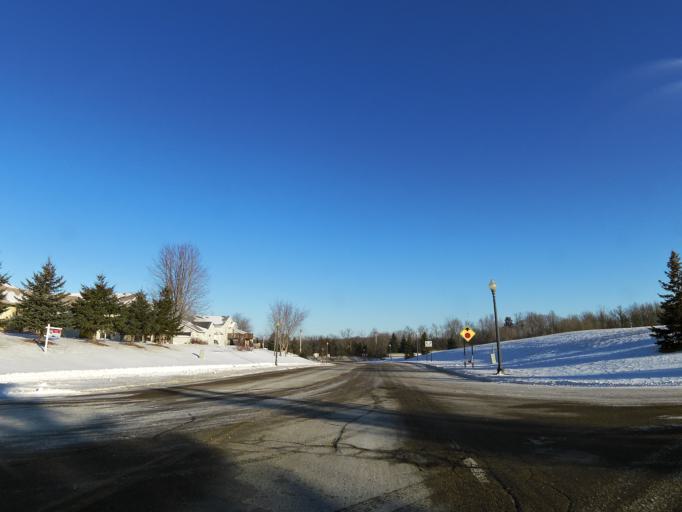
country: US
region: Minnesota
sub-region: Scott County
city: Jordan
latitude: 44.6654
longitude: -93.6133
